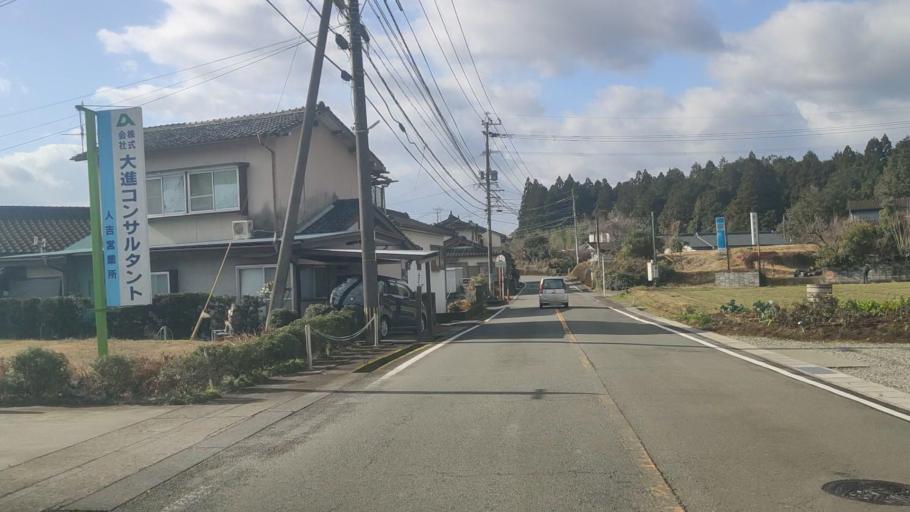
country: JP
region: Kumamoto
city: Hitoyoshi
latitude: 32.2321
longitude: 130.7866
